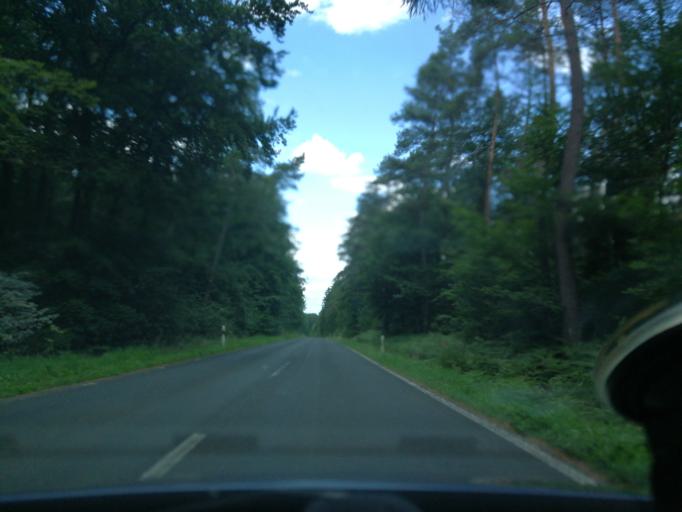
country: DE
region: Rheinland-Pfalz
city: Zemmer
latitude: 49.9163
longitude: 6.7033
